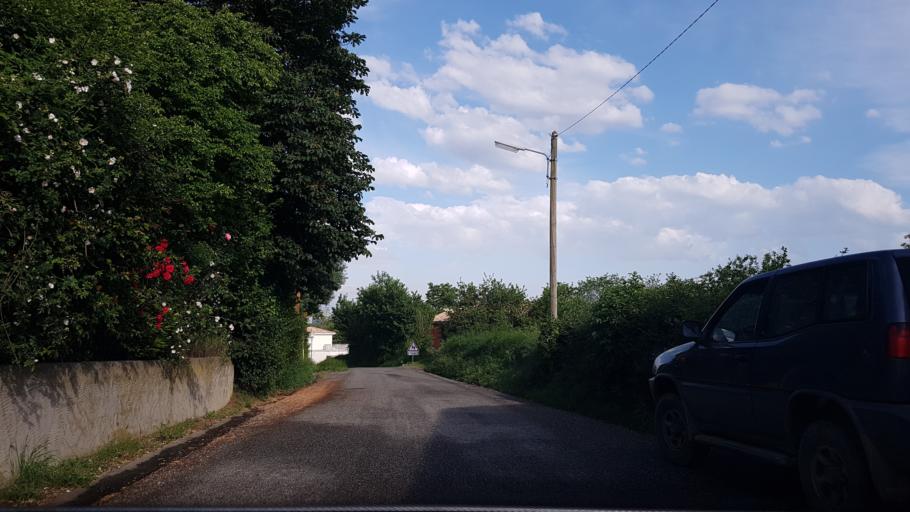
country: FR
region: Midi-Pyrenees
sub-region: Departement de l'Ariege
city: La Tour-du-Crieu
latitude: 43.1181
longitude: 1.7153
